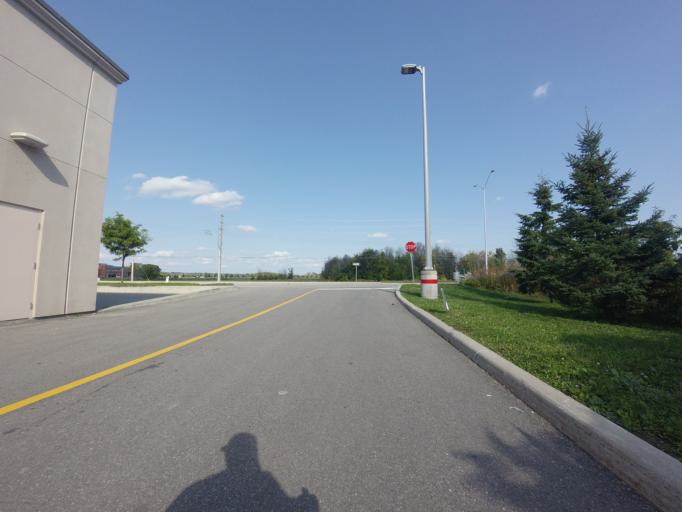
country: CA
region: Ontario
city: Ottawa
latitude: 45.2870
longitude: -75.6713
